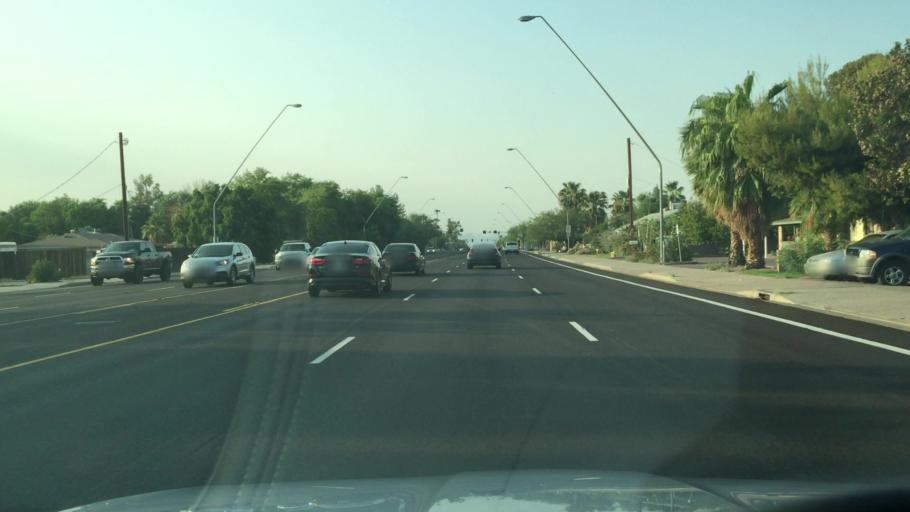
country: US
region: Arizona
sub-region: Maricopa County
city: Mesa
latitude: 33.4244
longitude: -111.8560
